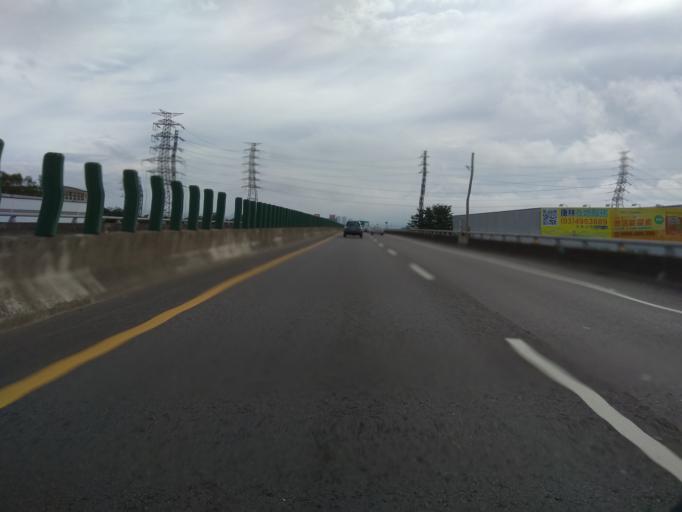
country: TW
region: Taiwan
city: Daxi
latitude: 24.8990
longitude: 121.2494
